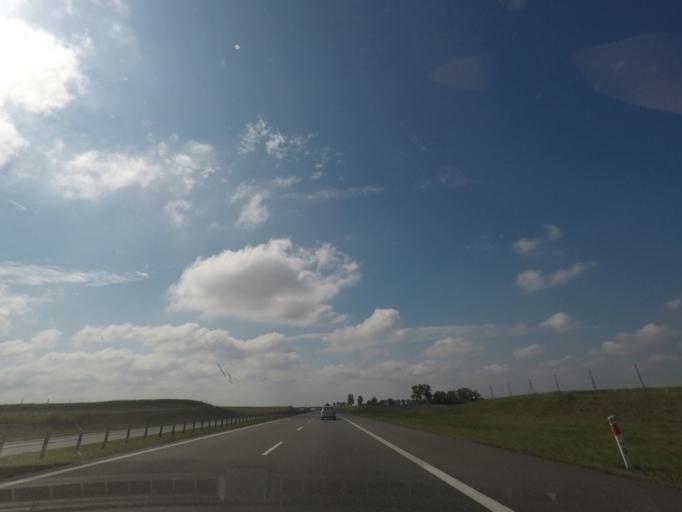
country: PL
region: Kujawsko-Pomorskie
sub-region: Powiat chelminski
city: Lisewo
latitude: 53.3161
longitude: 18.7063
